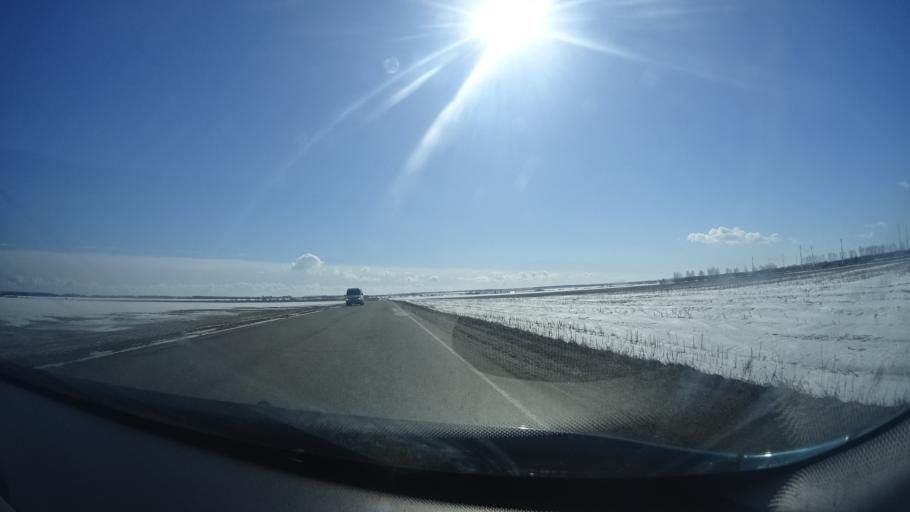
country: RU
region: Bashkortostan
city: Avdon
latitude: 54.6020
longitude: 55.8496
